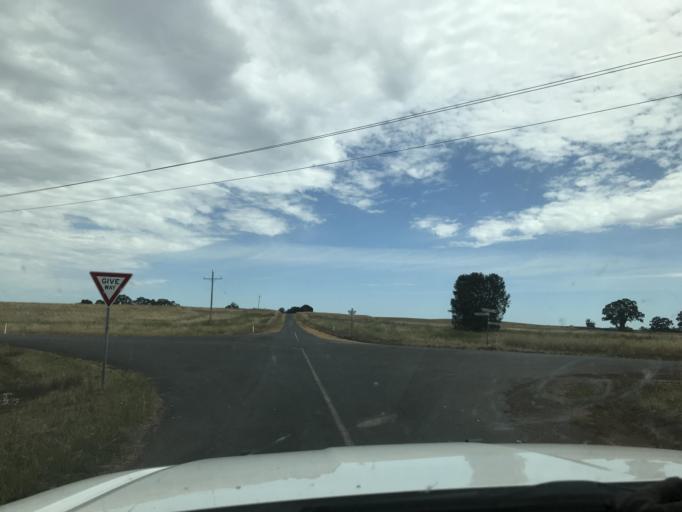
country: AU
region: Victoria
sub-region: Horsham
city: Horsham
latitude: -36.9934
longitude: 141.5470
